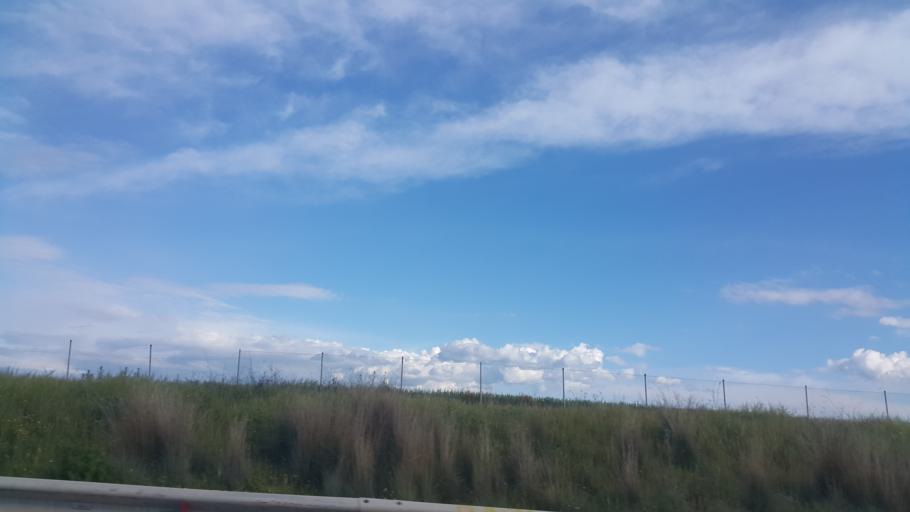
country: TR
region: Adana
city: Ceyhan
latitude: 37.0055
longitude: 35.9537
